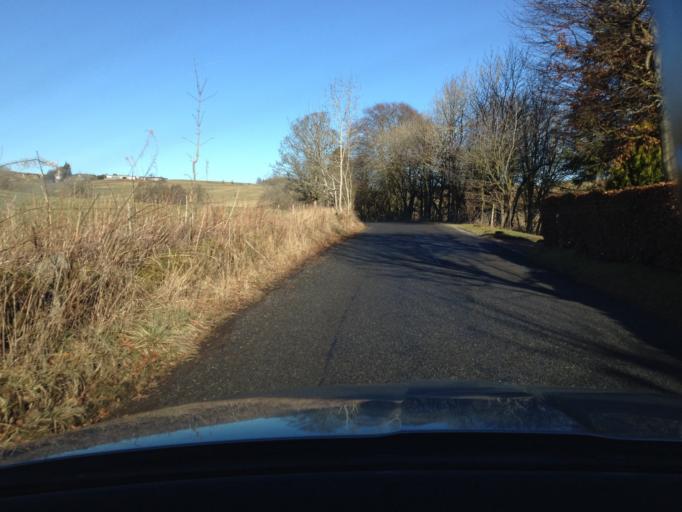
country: GB
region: Scotland
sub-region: Perth and Kinross
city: Bridge of Earn
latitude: 56.2919
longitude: -3.3965
